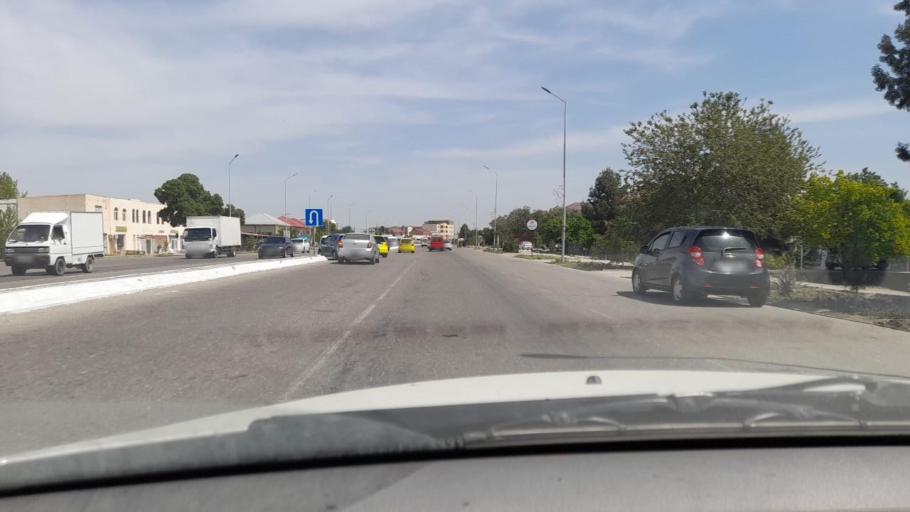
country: UZ
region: Bukhara
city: Galaosiyo
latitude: 39.8590
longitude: 64.4430
